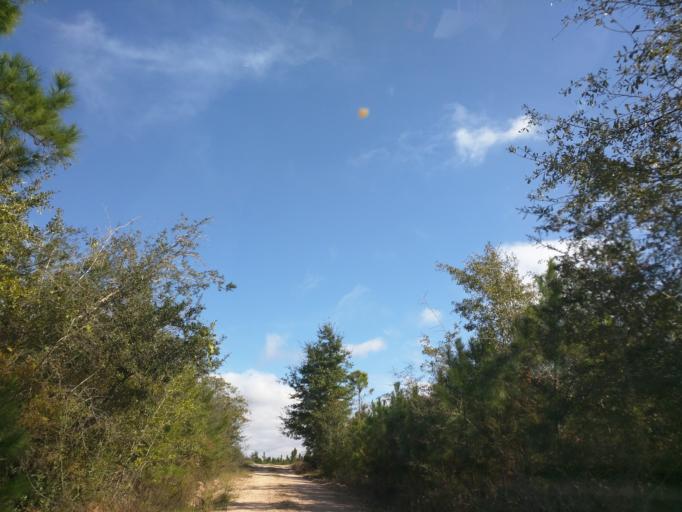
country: US
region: Florida
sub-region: Escambia County
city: Cantonment
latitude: 30.5512
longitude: -87.4233
